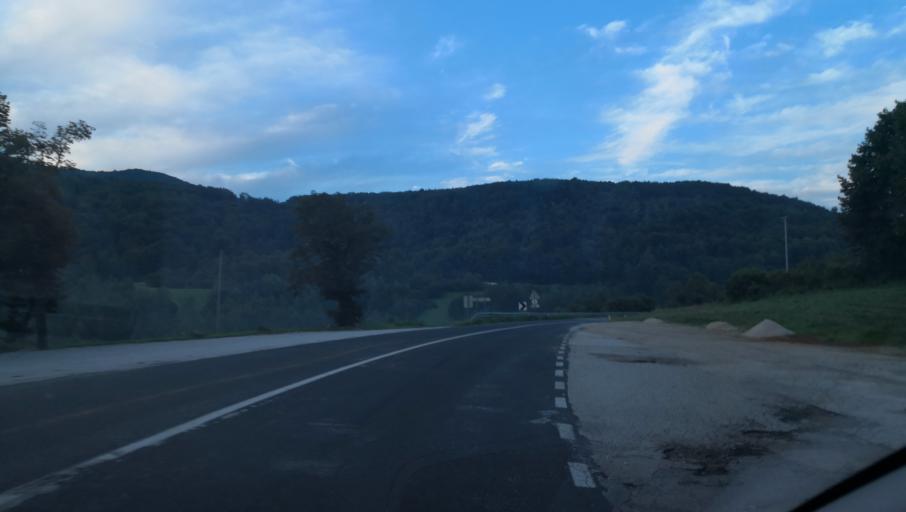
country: SI
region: Novo Mesto
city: Novo Mesto
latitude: 45.7400
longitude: 15.2227
